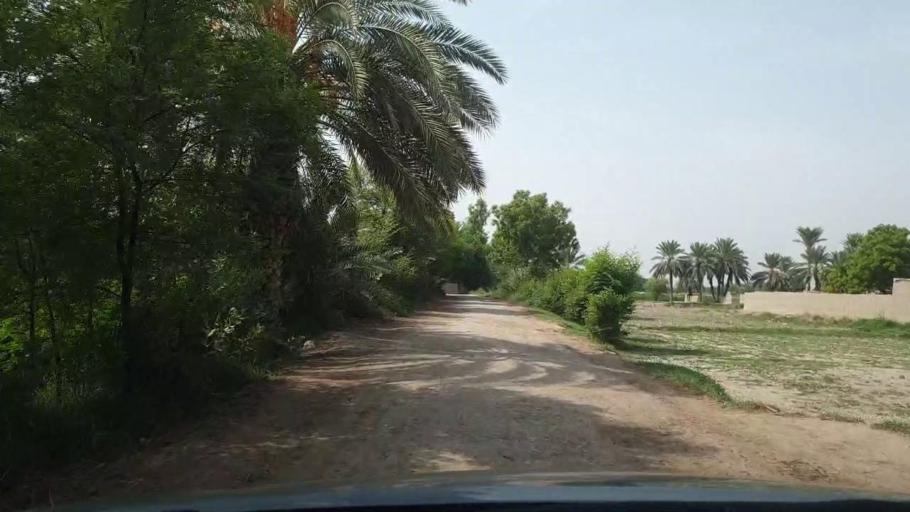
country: PK
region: Sindh
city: Rohri
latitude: 27.6542
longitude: 69.0103
